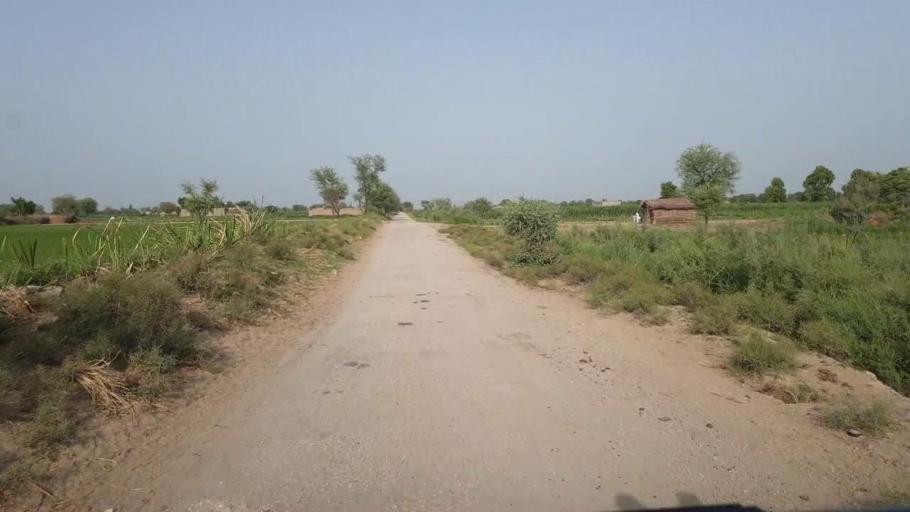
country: PK
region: Sindh
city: Daur
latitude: 26.3409
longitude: 68.1841
